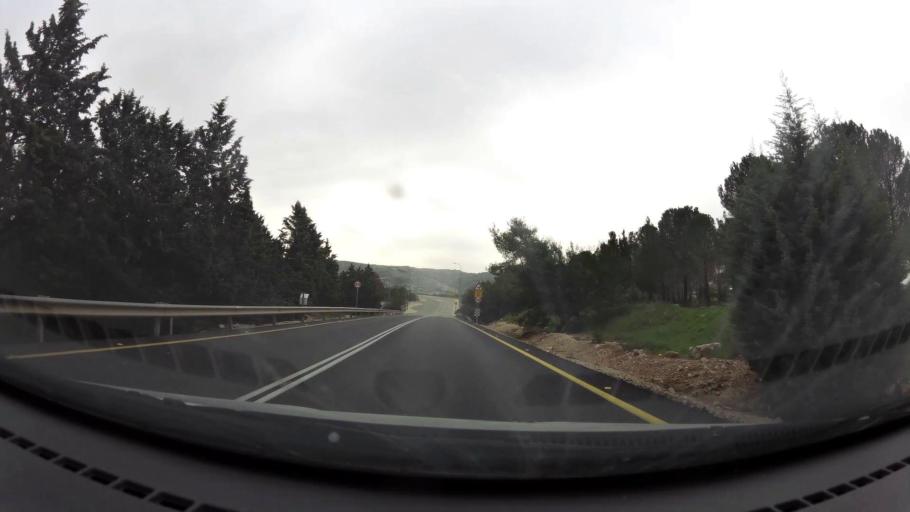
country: PS
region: West Bank
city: Surif
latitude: 31.6729
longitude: 35.0491
